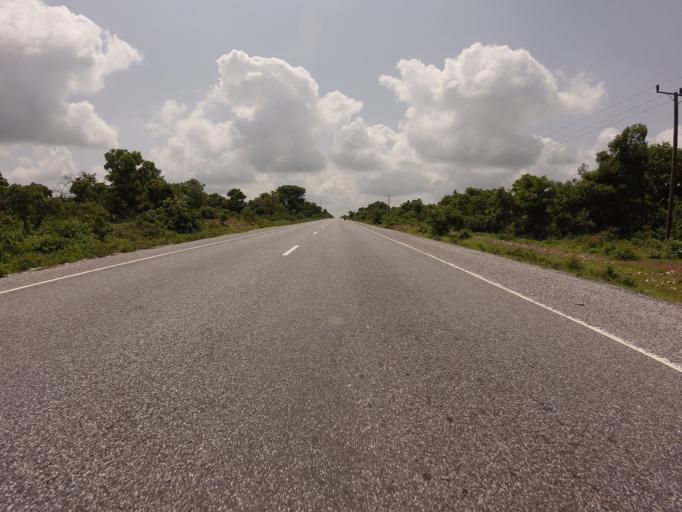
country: GH
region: Northern
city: Tamale
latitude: 9.1350
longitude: -1.5789
